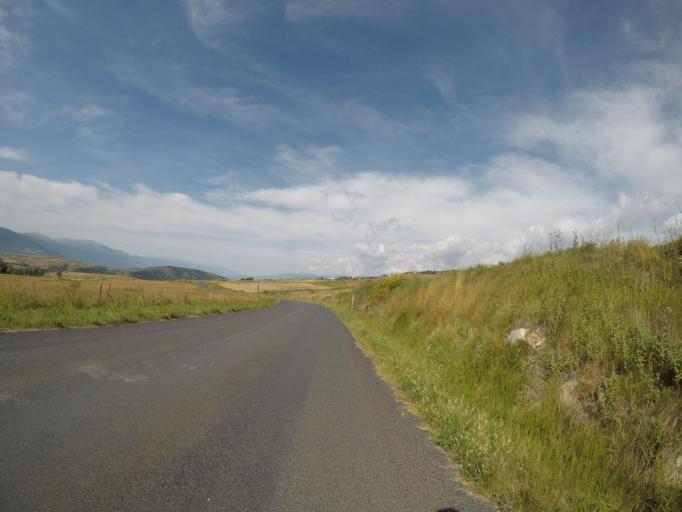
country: ES
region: Catalonia
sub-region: Provincia de Girona
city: Llivia
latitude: 42.5012
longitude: 2.0677
